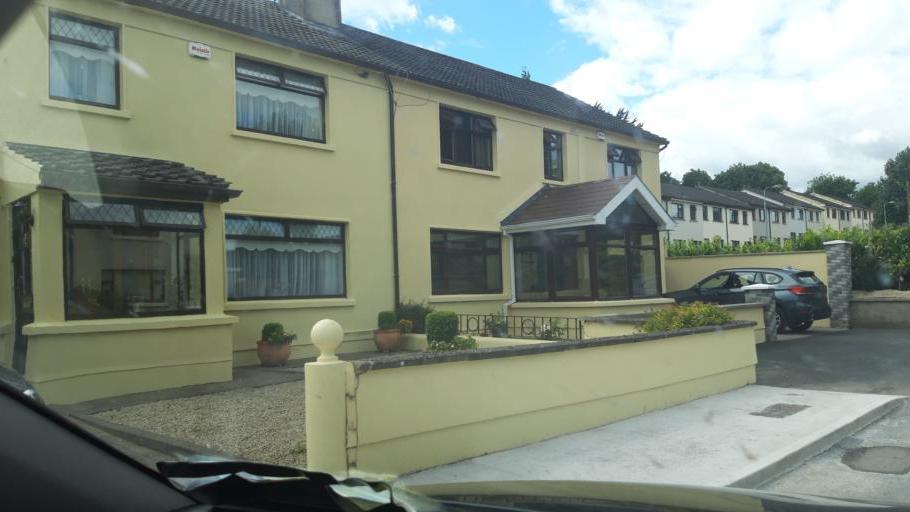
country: IE
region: Munster
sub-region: South Tipperary
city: Cluain Meala
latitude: 52.3475
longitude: -7.7038
